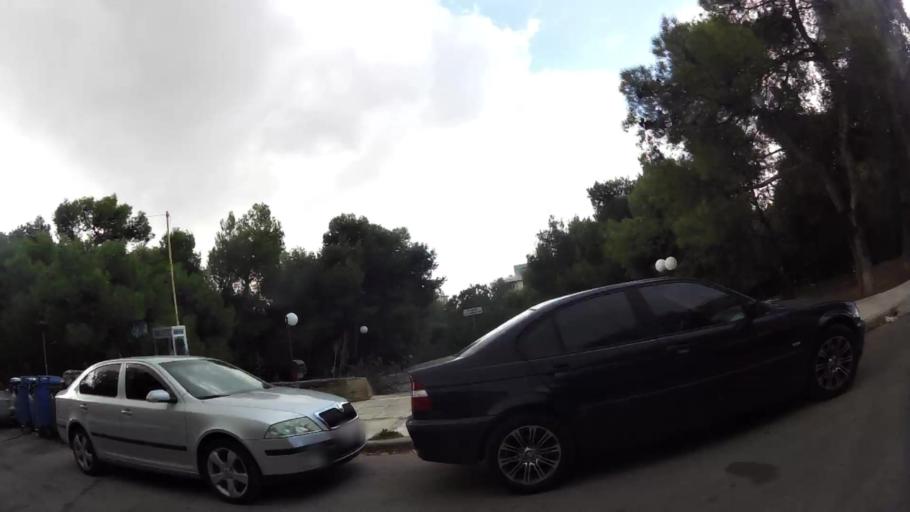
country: GR
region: Attica
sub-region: Nomarchia Athinas
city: Melissia
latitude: 38.0569
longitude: 23.8284
